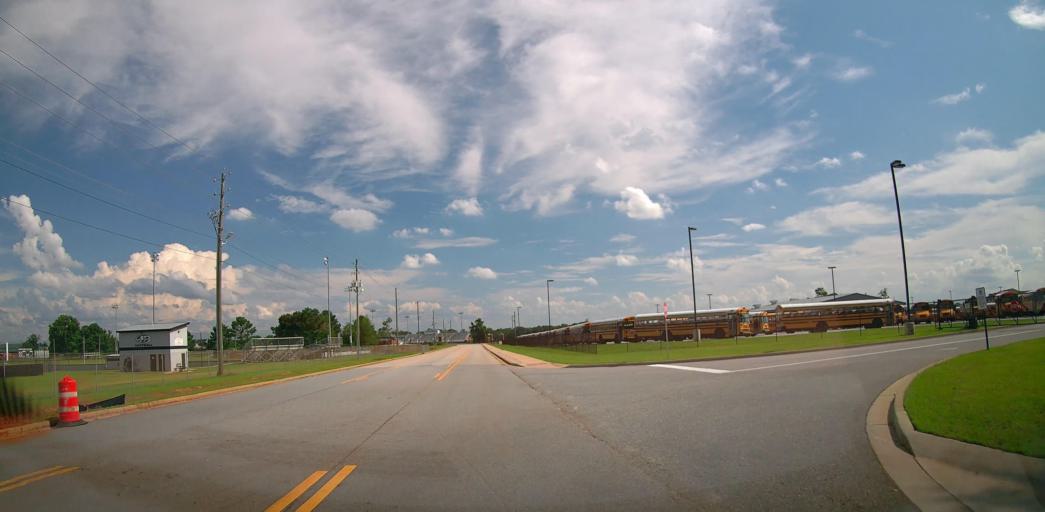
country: US
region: Georgia
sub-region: Houston County
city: Centerville
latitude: 32.5522
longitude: -83.6796
